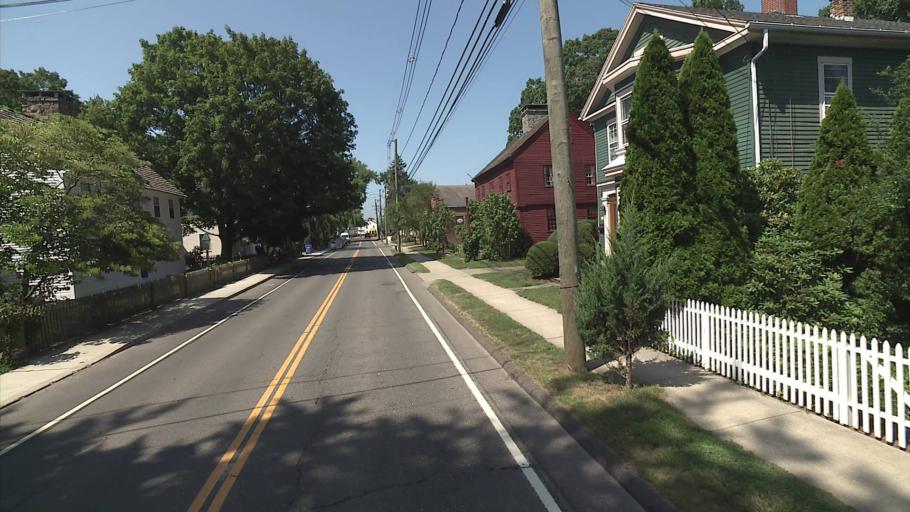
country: US
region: Connecticut
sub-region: New Haven County
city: Guilford Center
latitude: 41.2827
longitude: -72.6777
